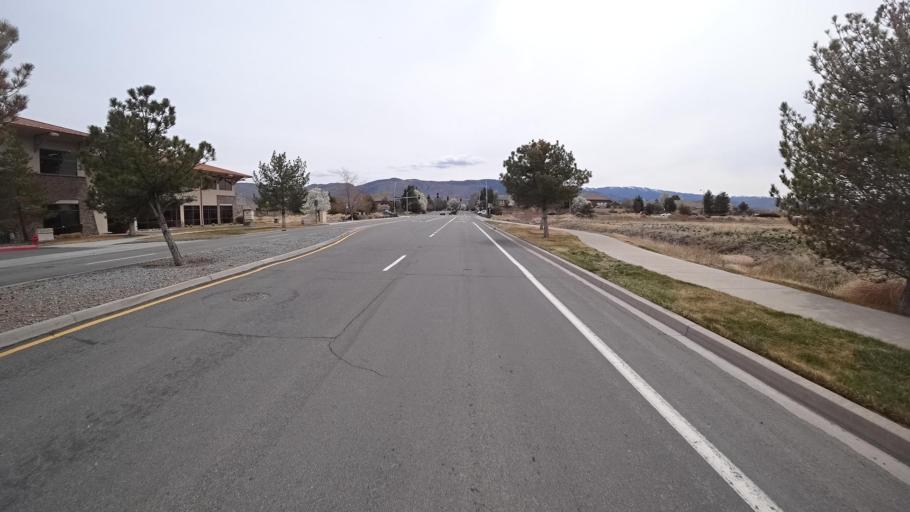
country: US
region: Nevada
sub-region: Washoe County
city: Sparks
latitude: 39.4444
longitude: -119.7469
